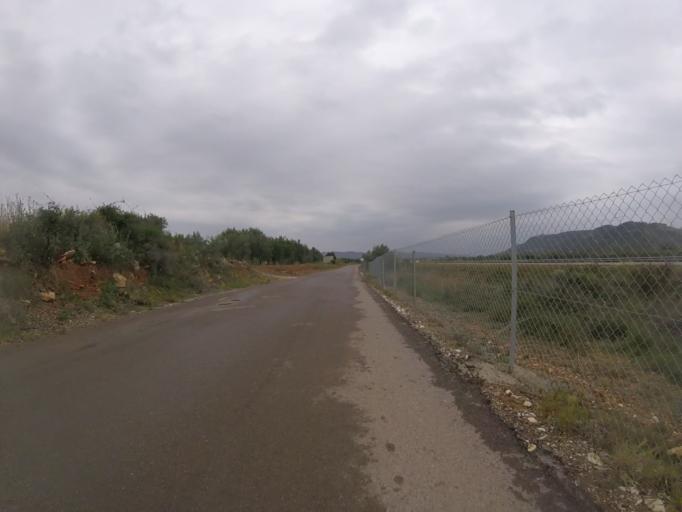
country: ES
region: Valencia
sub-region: Provincia de Castello
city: Alcala de Xivert
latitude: 40.2884
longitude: 0.2282
